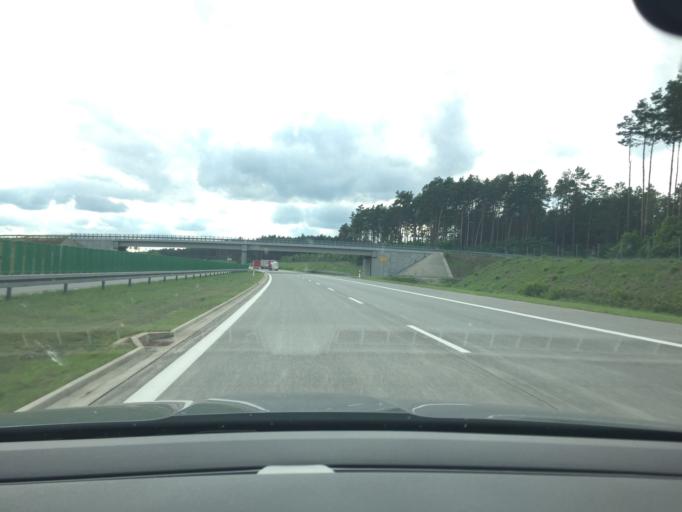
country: PL
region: Lubusz
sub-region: Powiat slubicki
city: Rzepin
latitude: 52.3385
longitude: 14.9542
